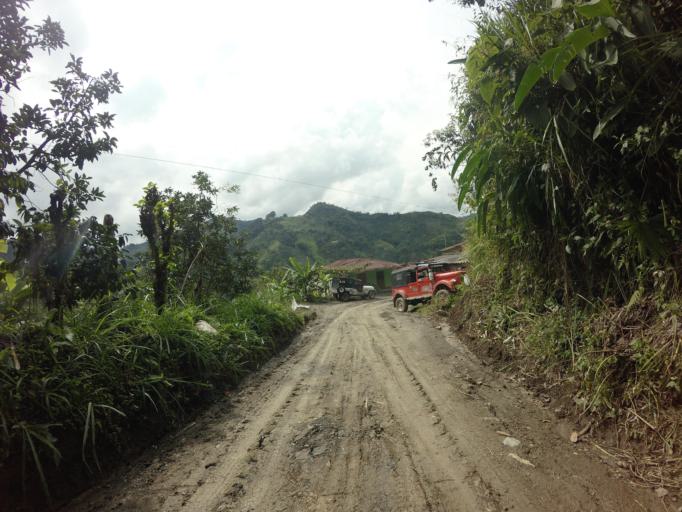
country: CO
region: Caldas
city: Marquetalia
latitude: 5.3246
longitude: -75.0446
